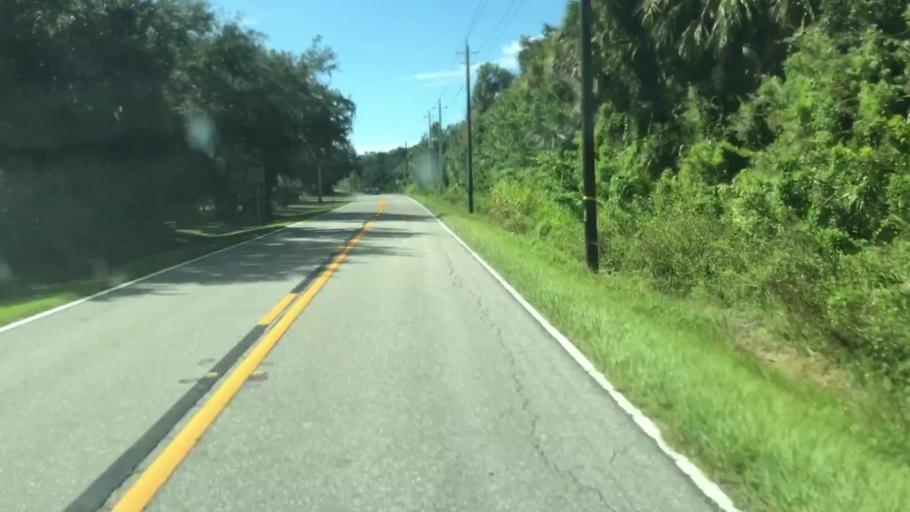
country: US
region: Florida
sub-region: Lee County
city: Alva
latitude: 26.7262
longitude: -81.6470
